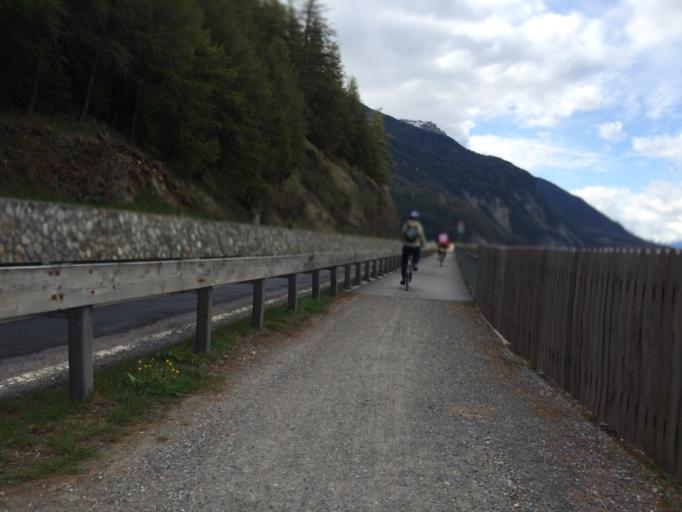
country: IT
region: Trentino-Alto Adige
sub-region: Bolzano
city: Curon Venosta
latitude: 46.8161
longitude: 10.5320
